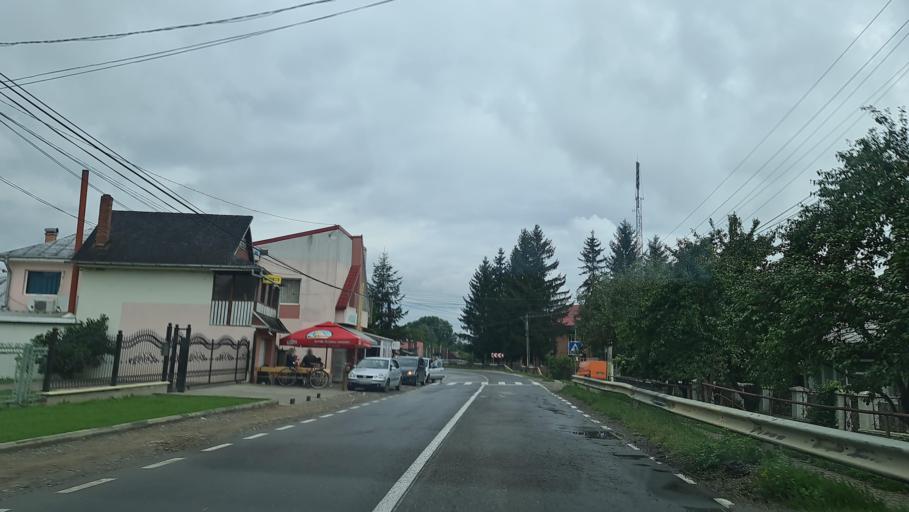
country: RO
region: Neamt
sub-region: Comuna Borlesti
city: Ruseni
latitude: 46.7975
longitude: 26.5379
